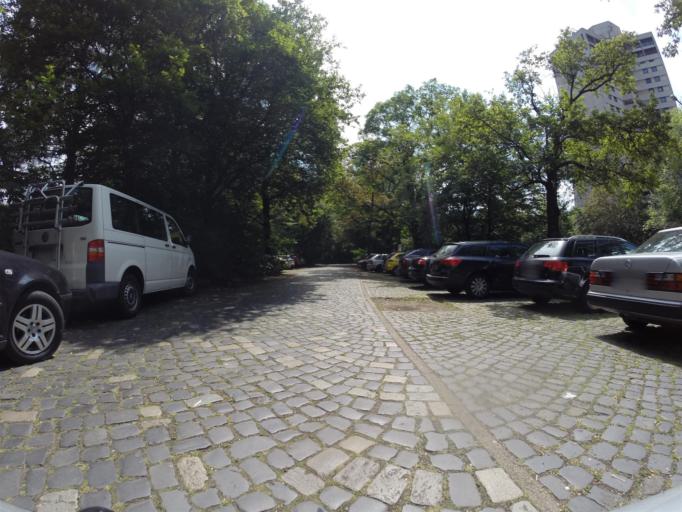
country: DE
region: Lower Saxony
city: Hannover
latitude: 52.3760
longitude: 9.7712
